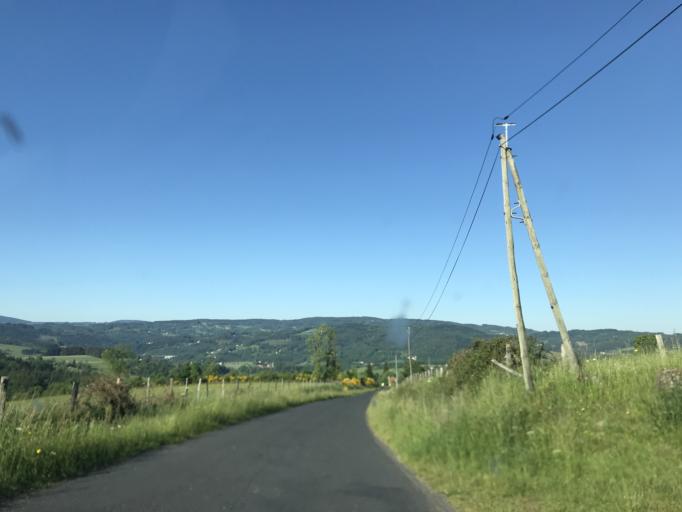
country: FR
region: Auvergne
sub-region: Departement du Puy-de-Dome
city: Job
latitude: 45.6652
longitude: 3.6928
